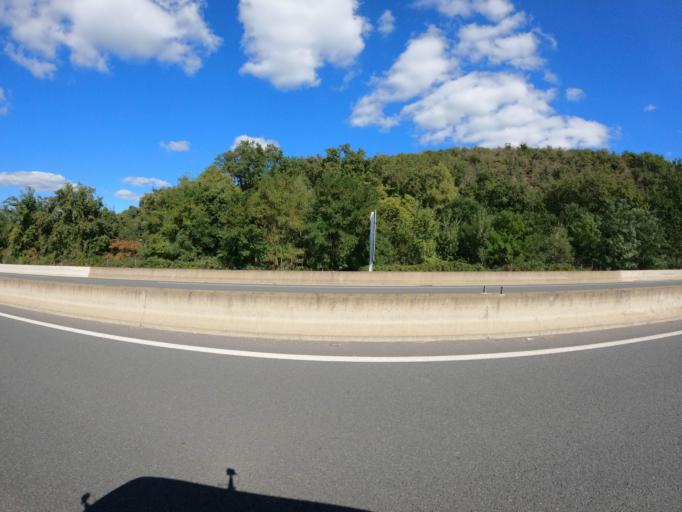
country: FR
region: Auvergne
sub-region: Departement de l'Allier
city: Desertines
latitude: 46.3770
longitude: 2.6284
